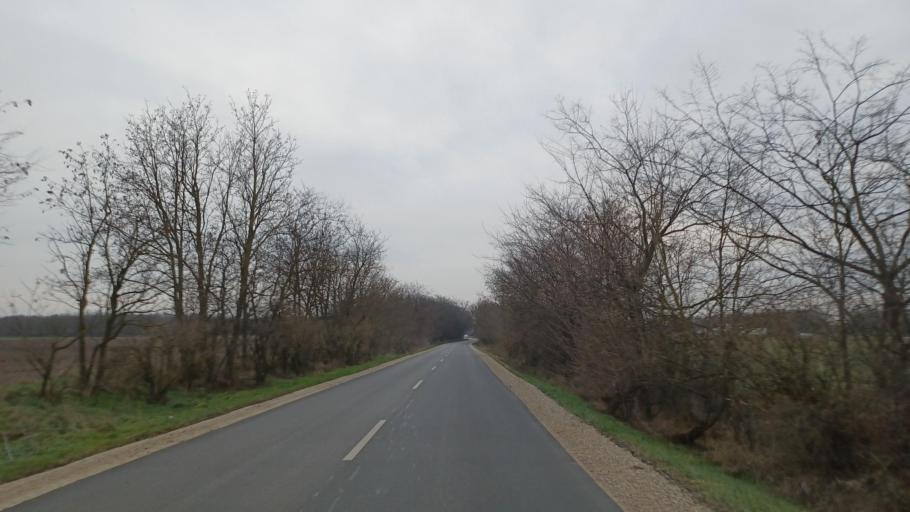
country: HU
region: Tolna
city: Nagydorog
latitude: 46.5744
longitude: 18.6344
